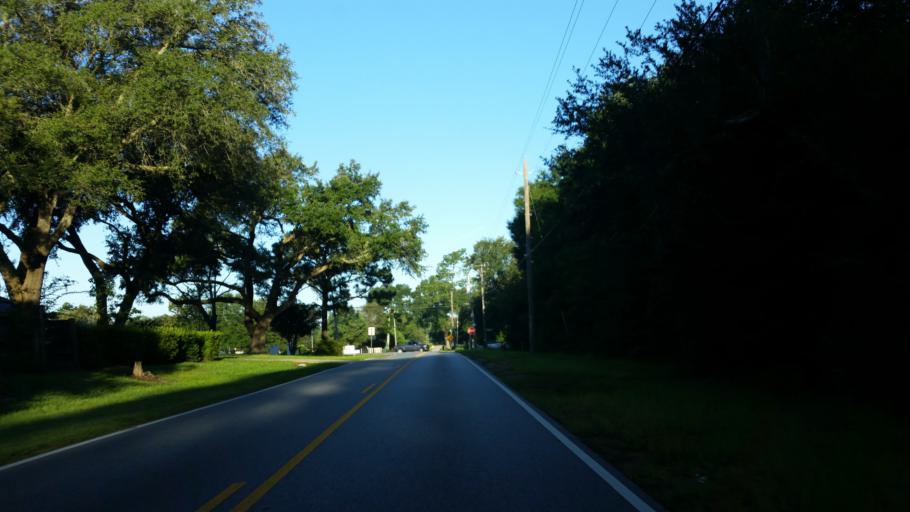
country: US
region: Florida
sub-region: Escambia County
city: Ensley
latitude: 30.5200
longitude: -87.3294
